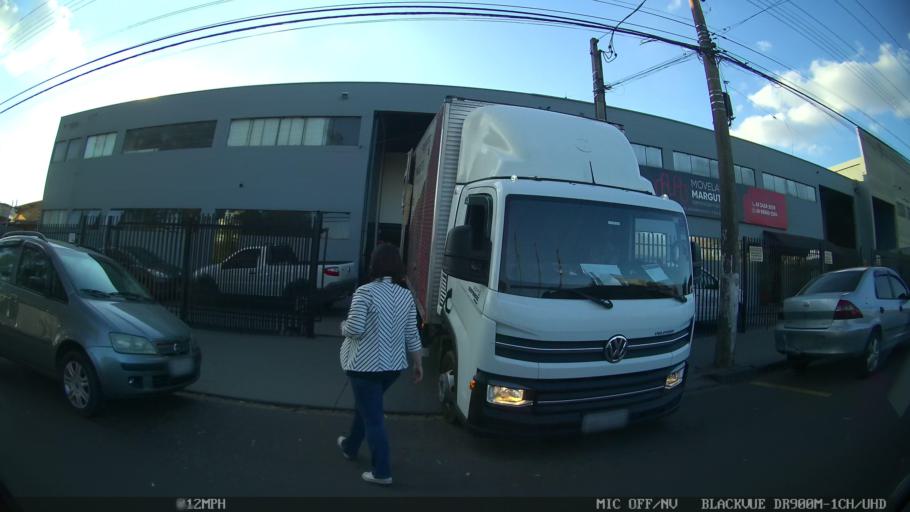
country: BR
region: Sao Paulo
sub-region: Santa Barbara D'Oeste
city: Santa Barbara d'Oeste
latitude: -22.7475
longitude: -47.3733
